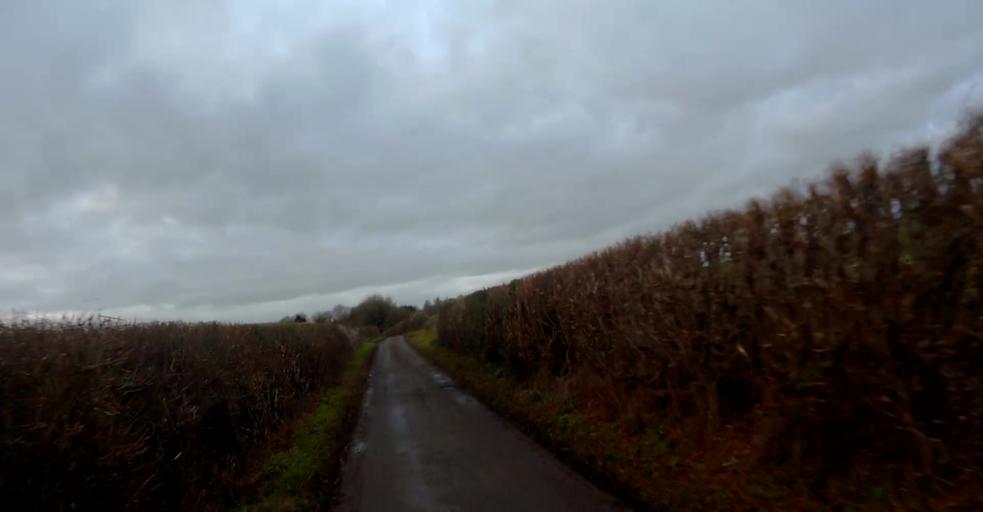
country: GB
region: England
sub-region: Hampshire
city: Overton
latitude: 51.2361
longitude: -1.2526
